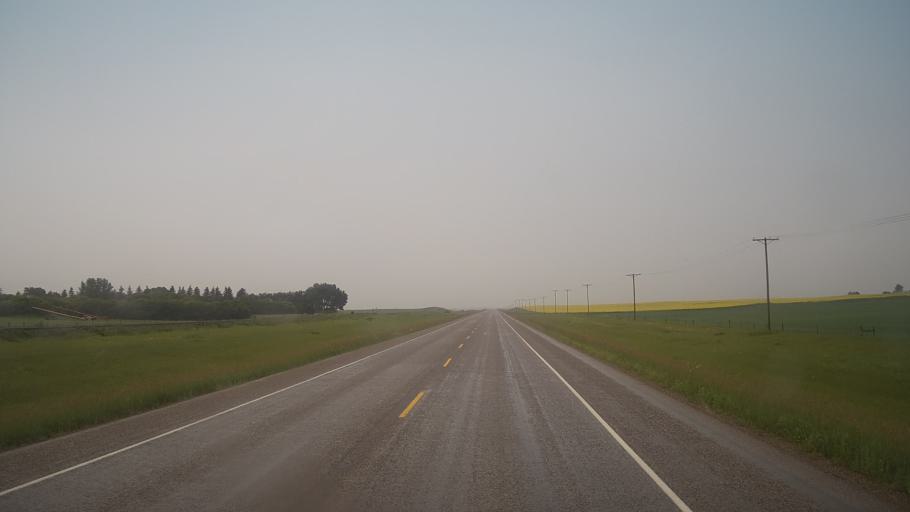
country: CA
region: Saskatchewan
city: Biggar
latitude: 52.1378
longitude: -108.1763
